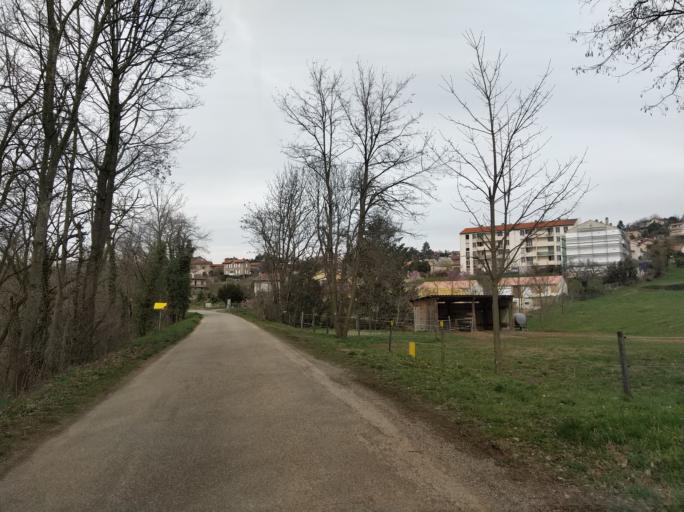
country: FR
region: Rhone-Alpes
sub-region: Departement de l'Ardeche
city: Boulieu-les-Annonay
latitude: 45.2685
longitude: 4.6620
